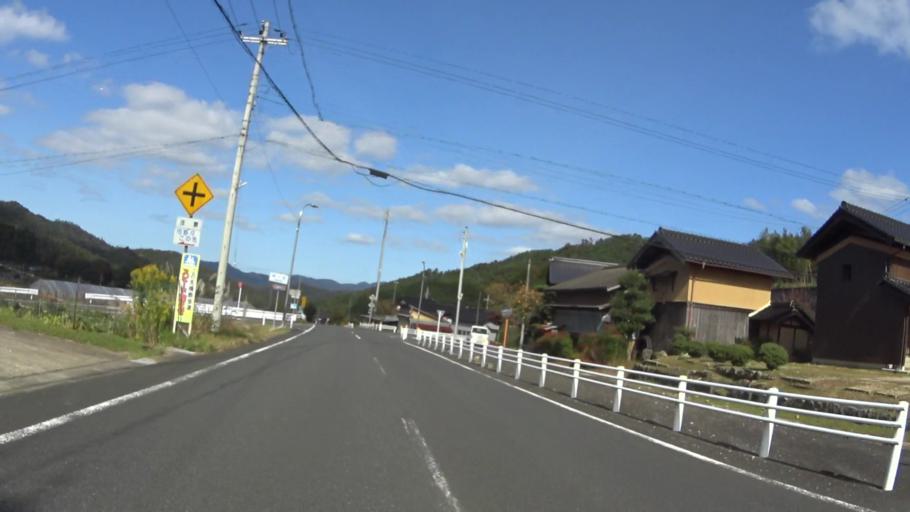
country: JP
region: Hyogo
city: Toyooka
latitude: 35.5441
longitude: 134.9780
